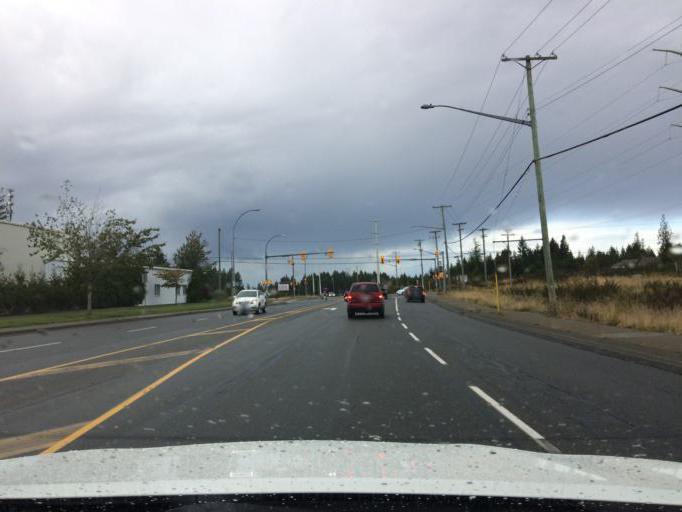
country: CA
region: British Columbia
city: Courtenay
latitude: 49.7144
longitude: -124.9706
